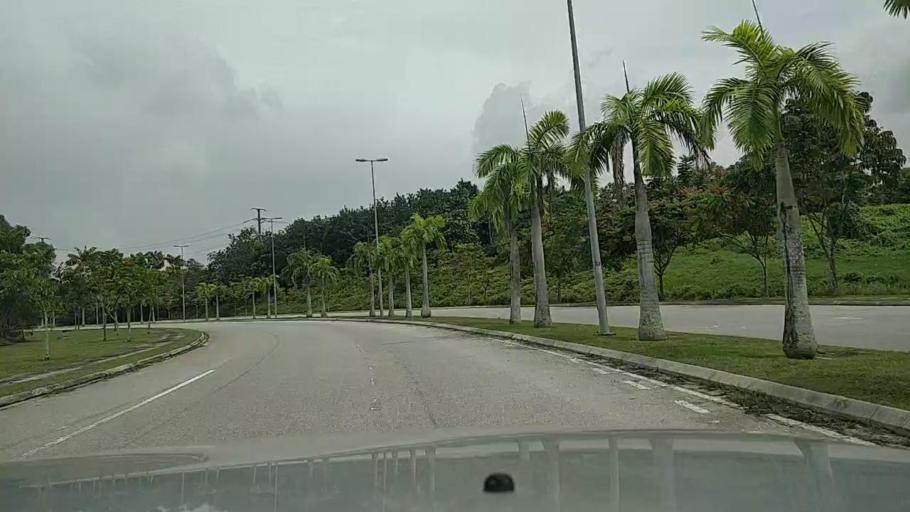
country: MY
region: Putrajaya
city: Putrajaya
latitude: 2.9019
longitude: 101.6514
